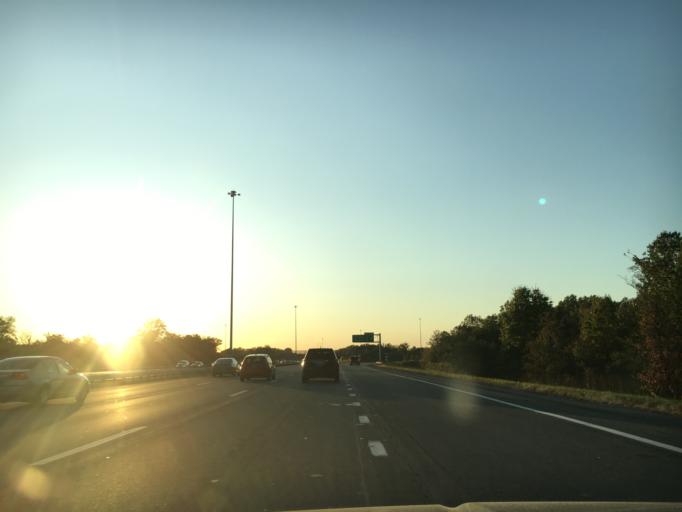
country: US
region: Ohio
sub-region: Cuyahoga County
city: Bay Village
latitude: 41.4681
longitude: -81.9445
